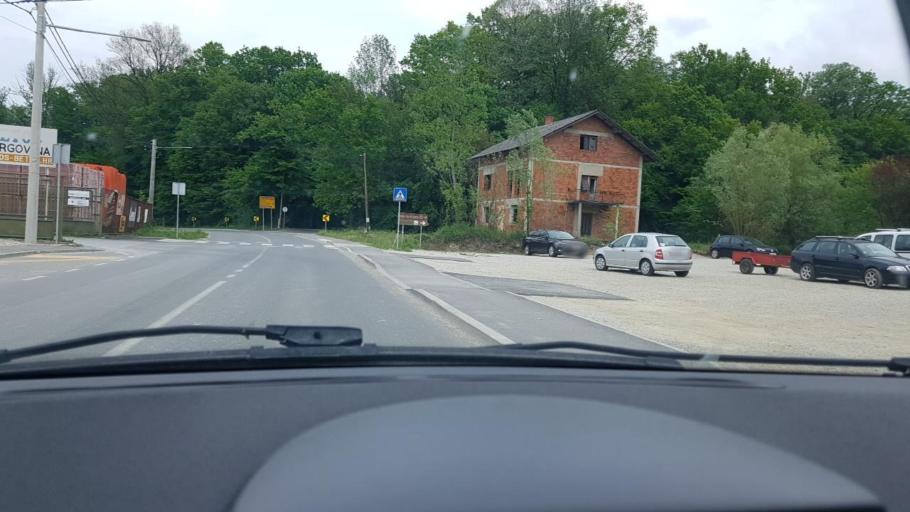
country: HR
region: Krapinsko-Zagorska
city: Bedekovcina
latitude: 45.9800
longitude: 15.9868
